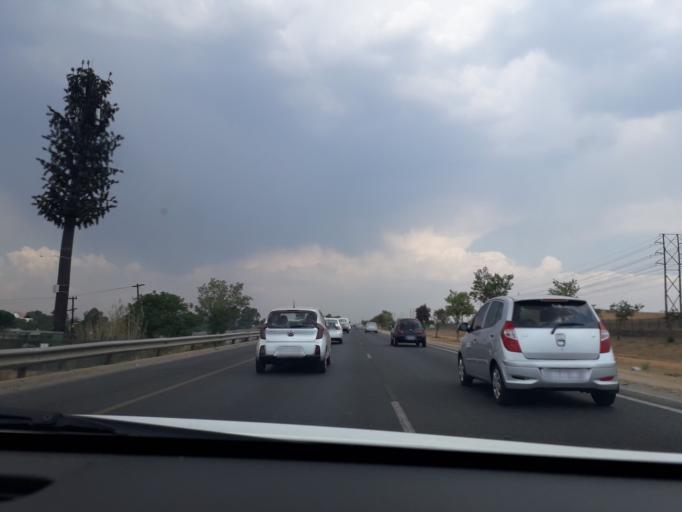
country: ZA
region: Gauteng
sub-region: City of Johannesburg Metropolitan Municipality
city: Midrand
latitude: -26.0283
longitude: 28.1330
